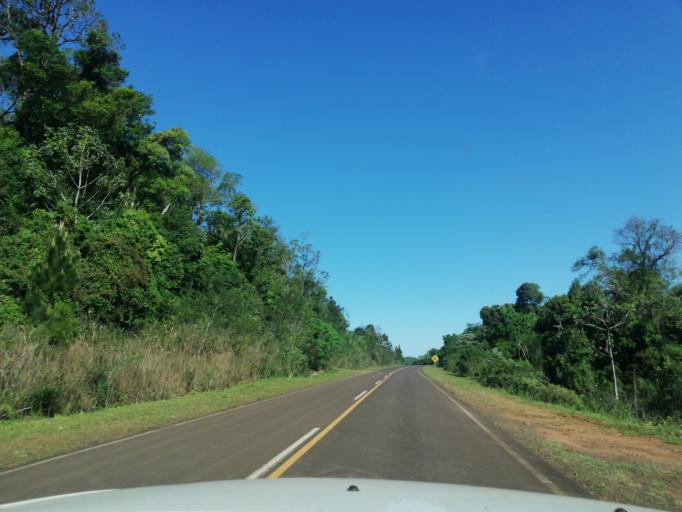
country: AR
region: Misiones
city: Arroyo del Medio
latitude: -27.6574
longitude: -55.4016
